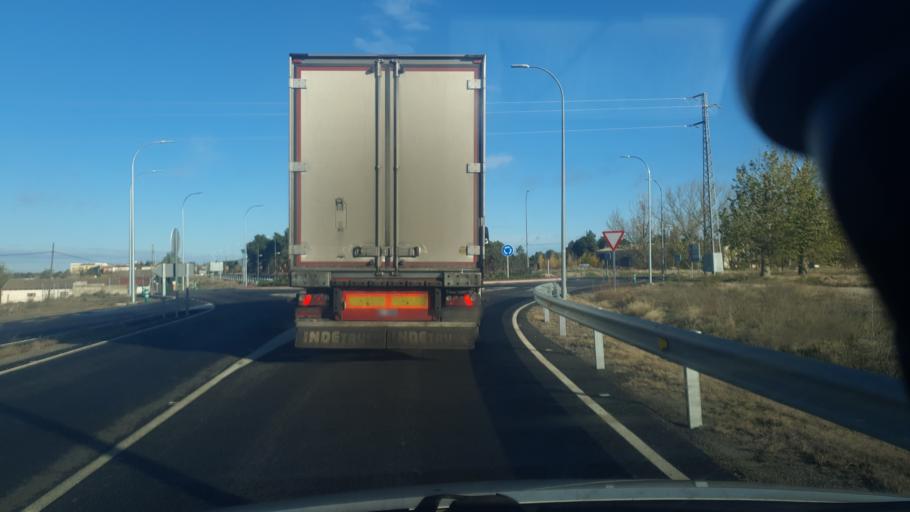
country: ES
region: Castille and Leon
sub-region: Provincia de Avila
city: Arevalo
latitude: 41.0444
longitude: -4.7167
